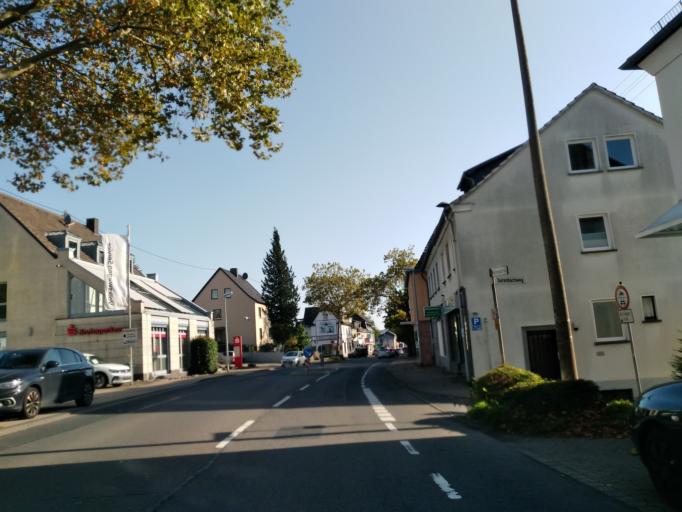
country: DE
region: Rheinland-Pfalz
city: Asbach
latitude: 50.7317
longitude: 7.3678
